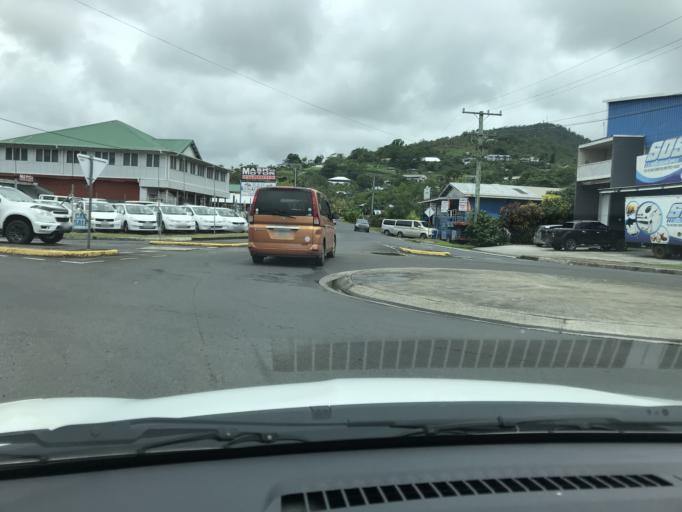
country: WS
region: Tuamasaga
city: Apia
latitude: -13.8369
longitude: -171.7680
